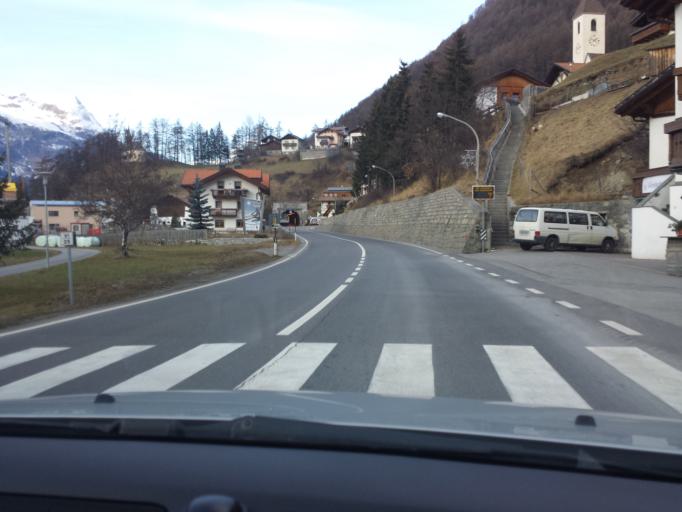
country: IT
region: Trentino-Alto Adige
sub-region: Bolzano
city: Curon Venosta
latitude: 46.8072
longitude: 10.5416
